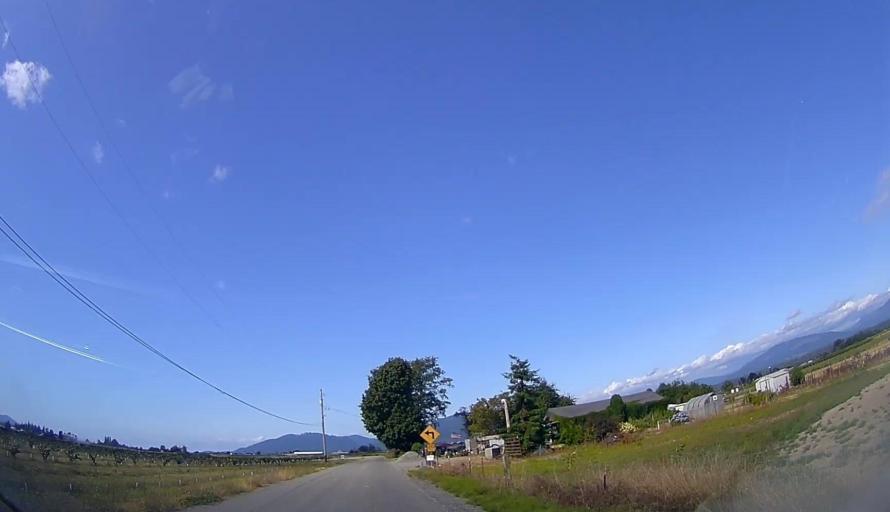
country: US
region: Washington
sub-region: Skagit County
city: Burlington
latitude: 48.5215
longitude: -122.4334
